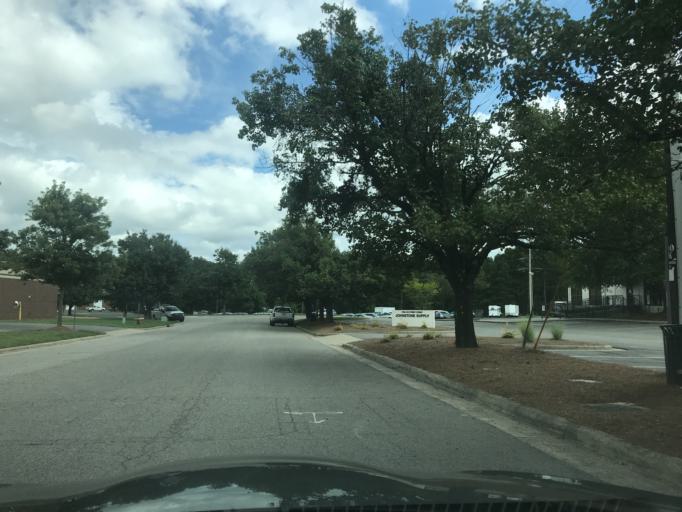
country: US
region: North Carolina
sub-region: Wake County
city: Raleigh
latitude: 35.8215
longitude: -78.6156
